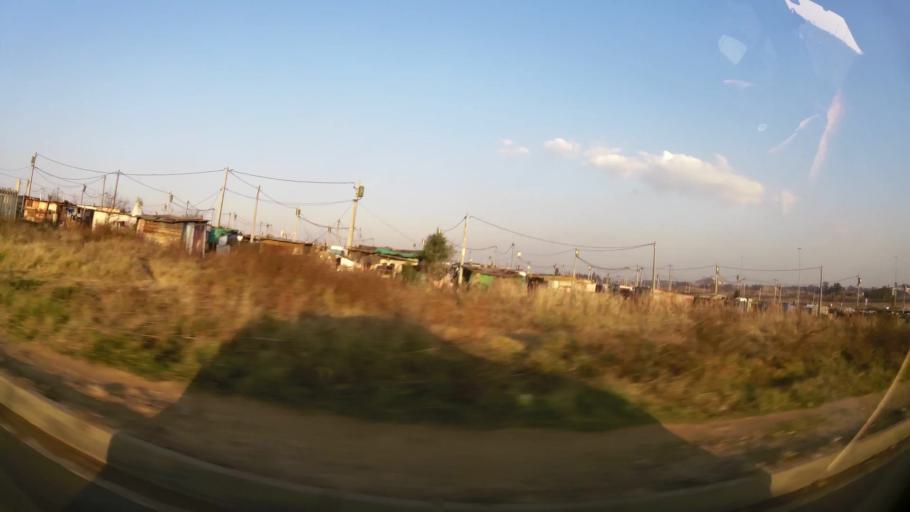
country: ZA
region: Gauteng
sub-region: Ekurhuleni Metropolitan Municipality
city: Benoni
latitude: -26.1631
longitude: 28.3713
